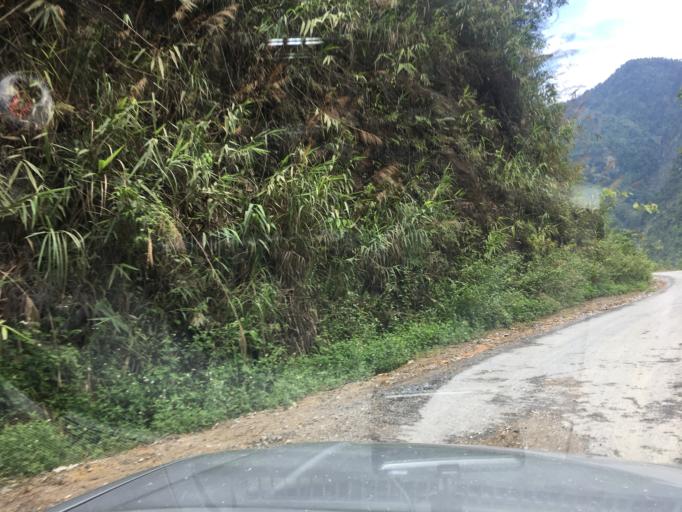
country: VN
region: Yen Bai
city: Son Thinh
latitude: 21.6846
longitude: 104.5739
